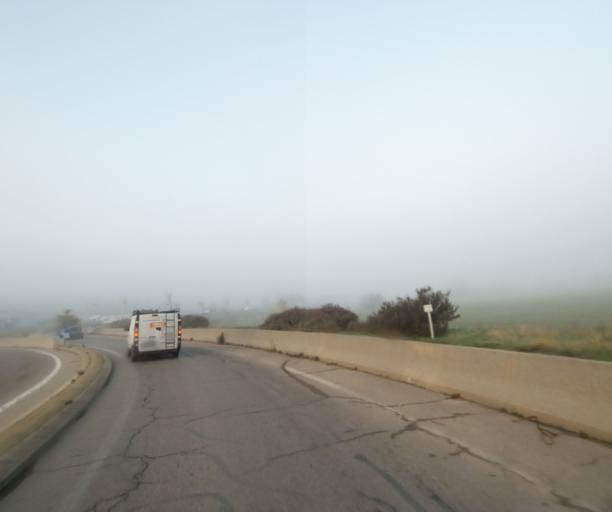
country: FR
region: Provence-Alpes-Cote d'Azur
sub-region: Departement des Bouches-du-Rhone
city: Meyreuil
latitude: 43.4744
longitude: 5.4814
